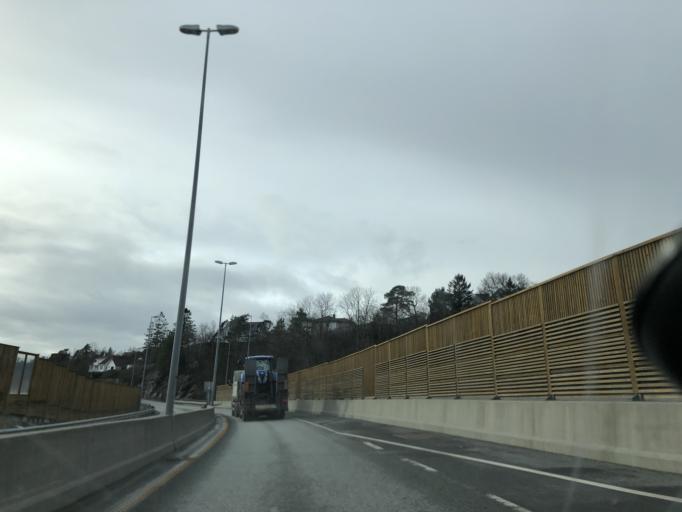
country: NO
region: Rogaland
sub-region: Tysvaer
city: Aksdal
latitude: 59.5052
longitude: 5.5901
